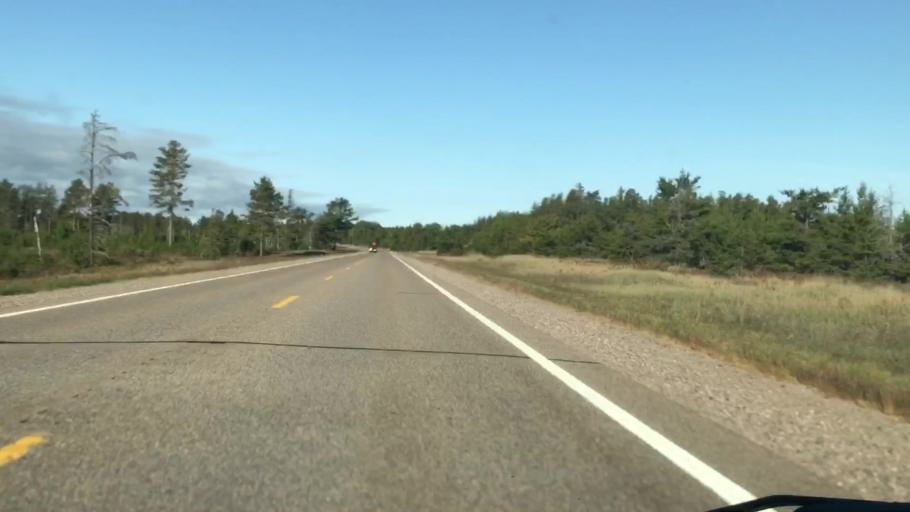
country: US
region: Michigan
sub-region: Mackinac County
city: Saint Ignace
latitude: 46.3583
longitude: -84.8796
